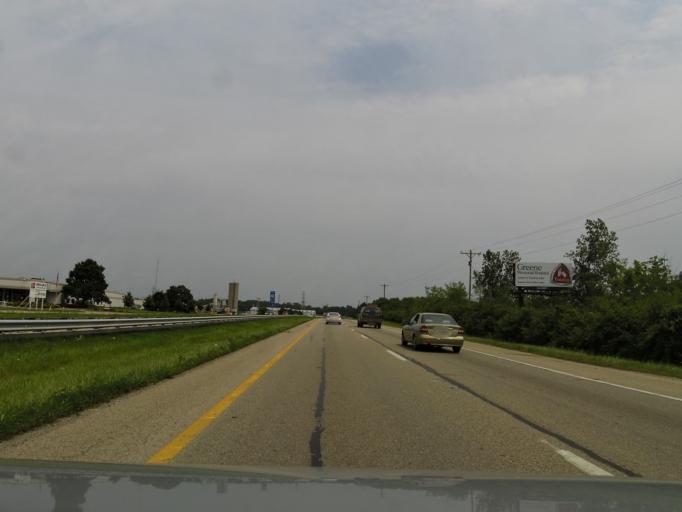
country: US
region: Ohio
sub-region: Greene County
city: Beavercreek
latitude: 39.7052
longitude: -84.0141
